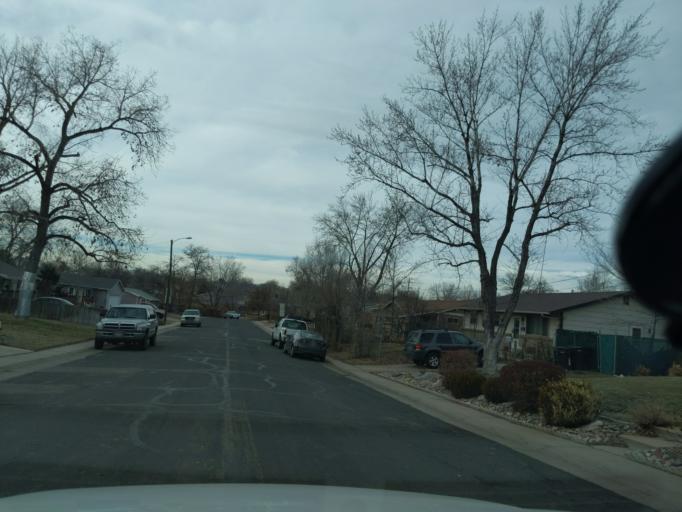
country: US
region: Colorado
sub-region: Adams County
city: Thornton
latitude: 39.8601
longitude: -104.9537
